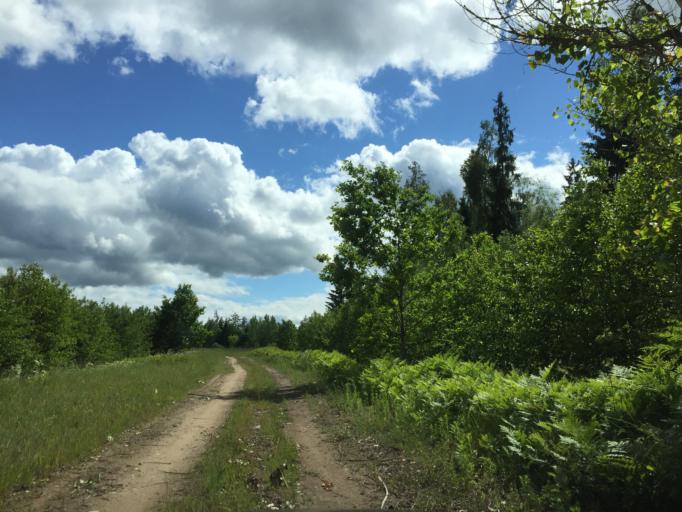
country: LV
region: Lecava
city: Iecava
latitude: 56.5514
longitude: 24.3420
